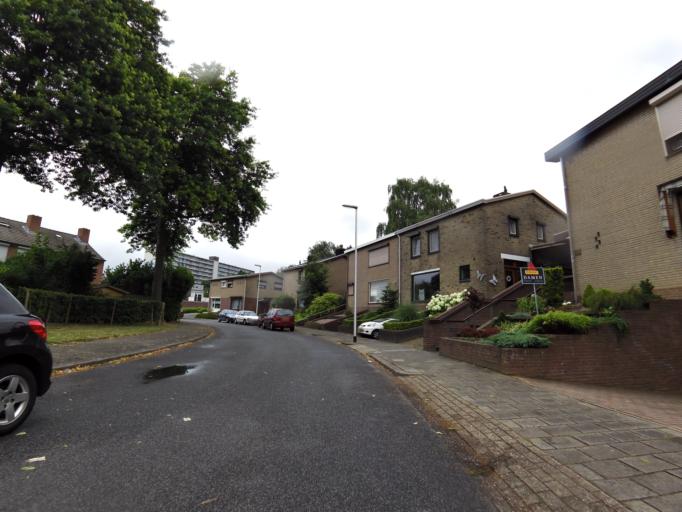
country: NL
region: Limburg
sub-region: Gemeente Heerlen
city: Heerlen
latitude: 50.8664
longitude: 6.0092
